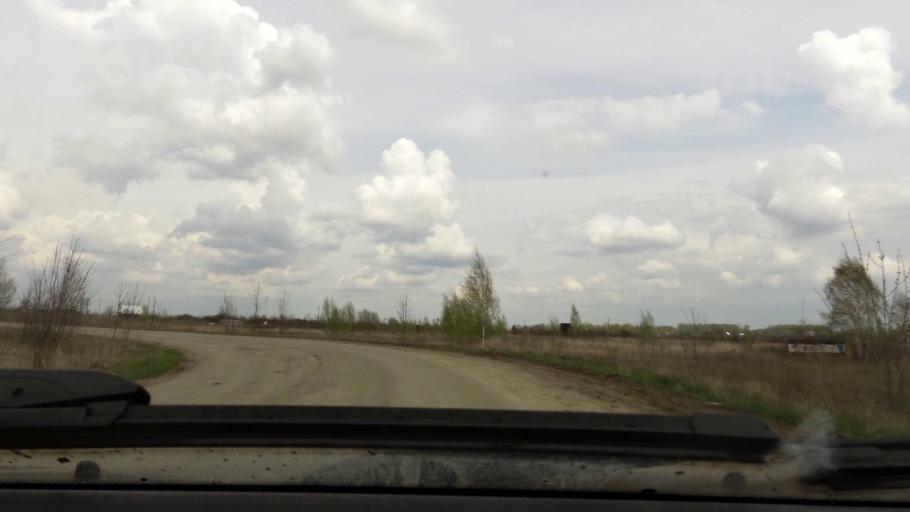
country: RU
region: Rjazan
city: Bagramovo
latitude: 54.7045
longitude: 39.3175
